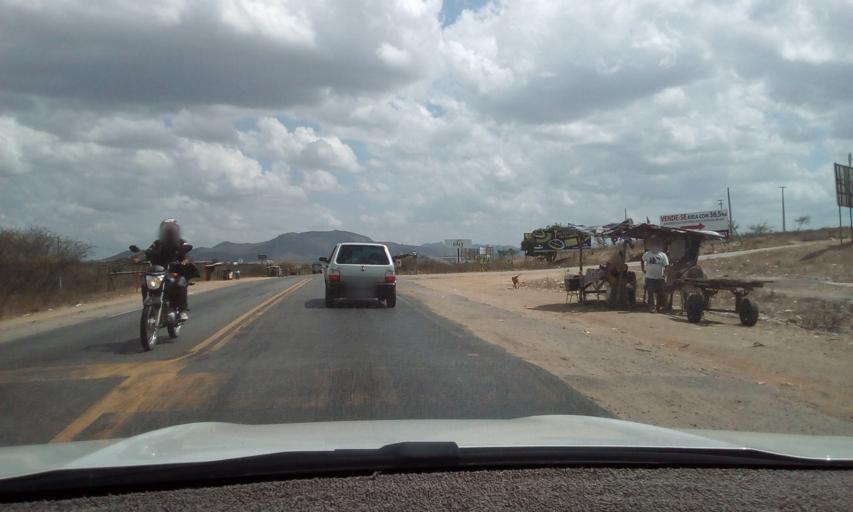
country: BR
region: Pernambuco
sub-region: Toritama
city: Toritama
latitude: -8.0243
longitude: -36.0531
